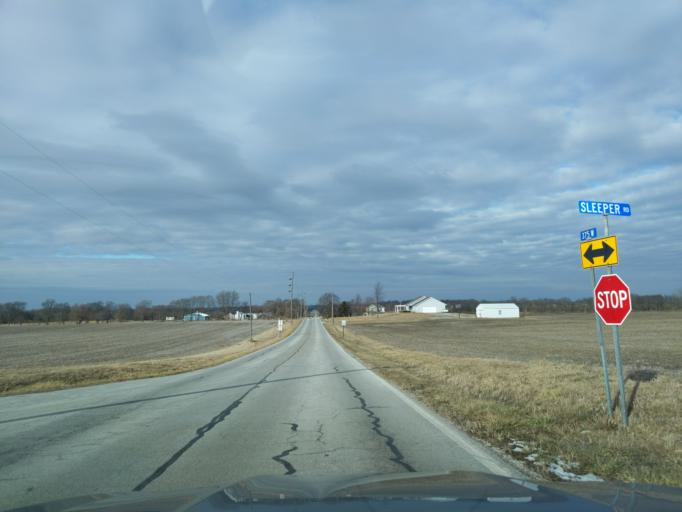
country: US
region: Indiana
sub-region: Tippecanoe County
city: Shadeland
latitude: 40.3411
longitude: -86.9755
